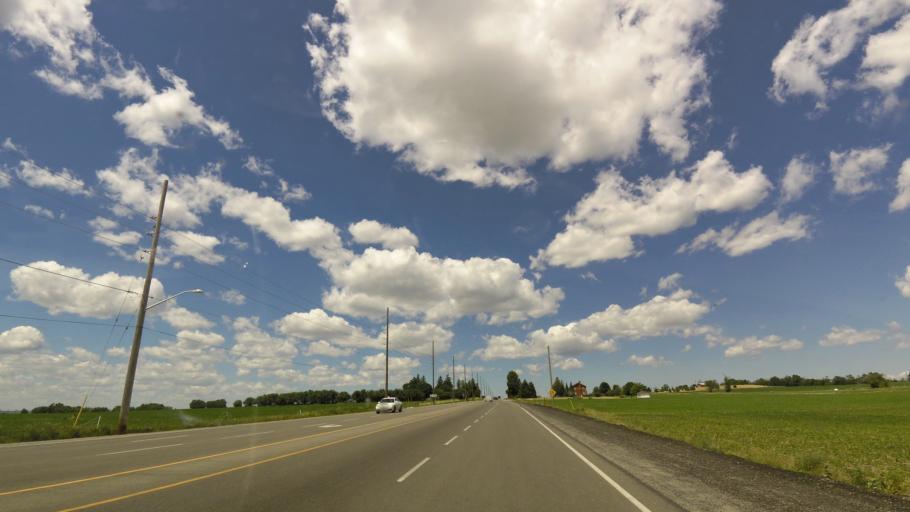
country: CA
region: Ontario
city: Oshawa
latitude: 43.9576
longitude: -78.8574
